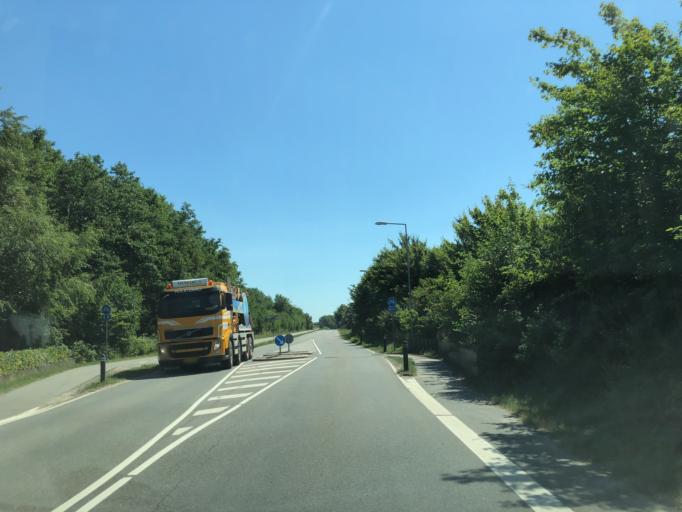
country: DK
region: Central Jutland
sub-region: Holstebro Kommune
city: Holstebro
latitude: 56.3454
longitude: 8.6595
